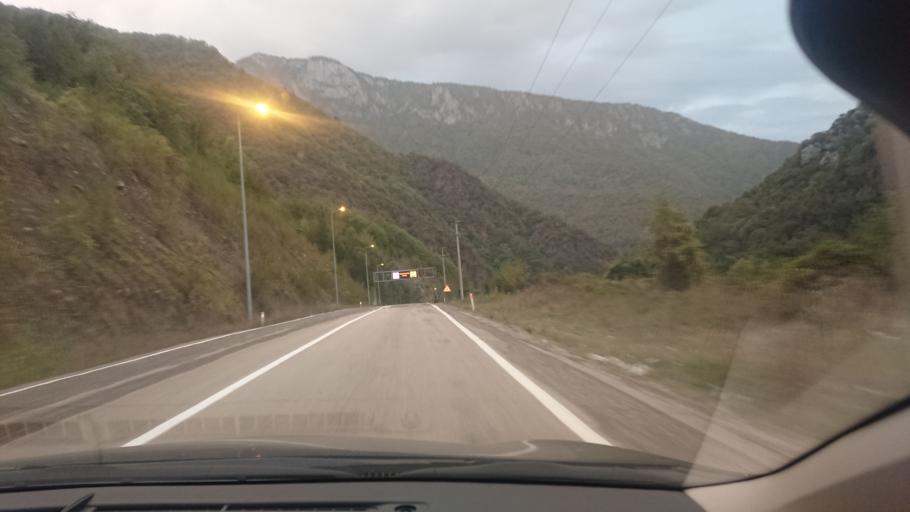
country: TR
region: Karabuk
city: Yenice
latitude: 41.1571
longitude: 32.4677
